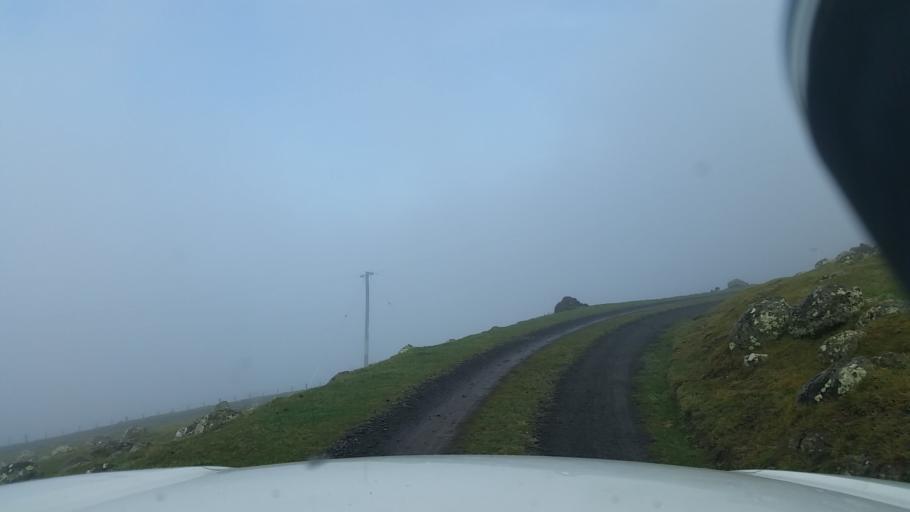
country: NZ
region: Canterbury
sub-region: Christchurch City
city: Christchurch
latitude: -43.6587
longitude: 172.8787
